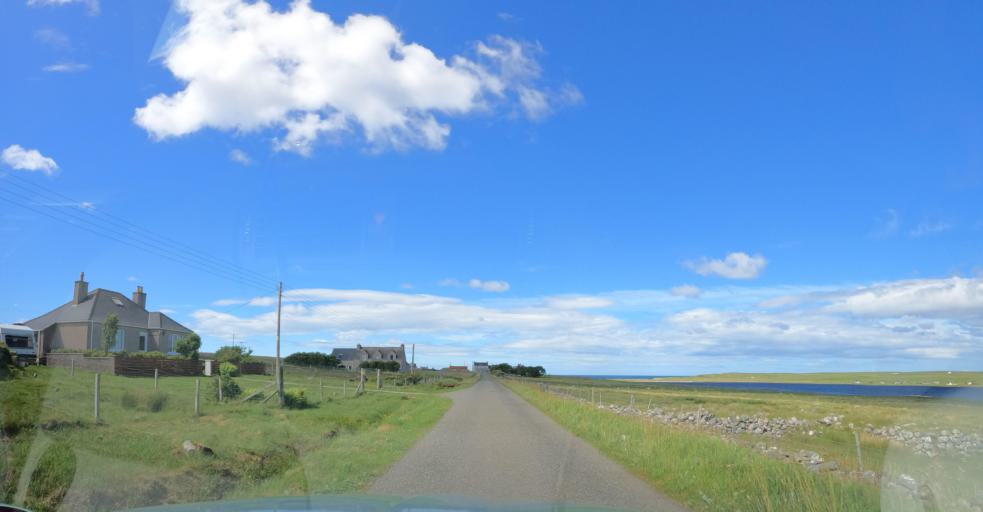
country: GB
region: Scotland
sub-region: Eilean Siar
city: Isle of Lewis
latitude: 58.3513
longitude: -6.5466
